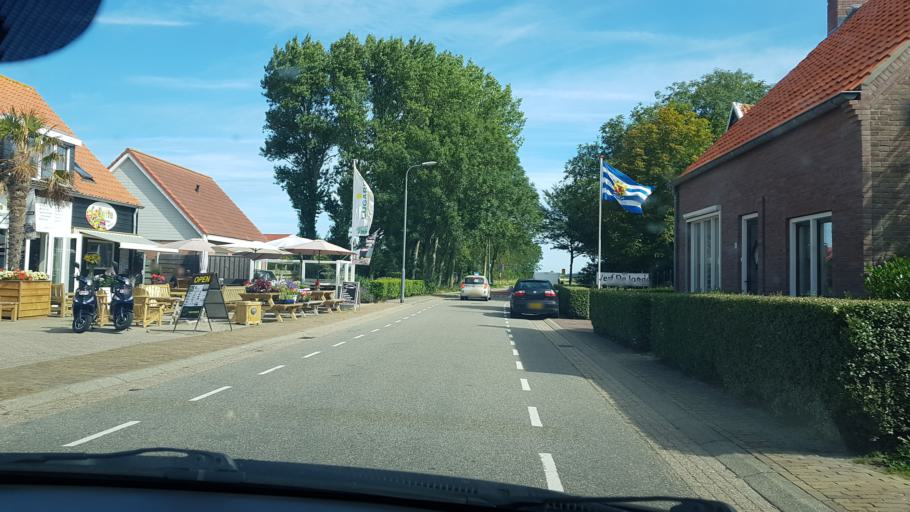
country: NL
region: Zeeland
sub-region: Gemeente Vlissingen
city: Vlissingen
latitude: 51.5166
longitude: 3.5109
